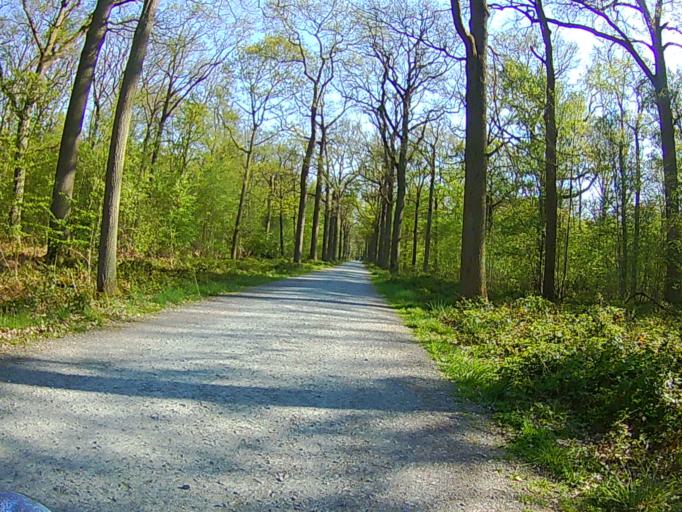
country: BE
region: Flanders
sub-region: Provincie Antwerpen
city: Brasschaat
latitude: 51.2741
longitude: 4.4844
